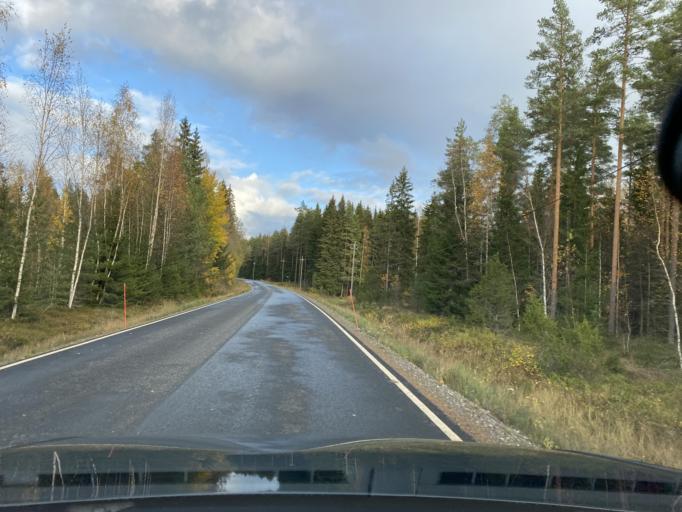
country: FI
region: Pirkanmaa
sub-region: Lounais-Pirkanmaa
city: Punkalaidun
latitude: 61.0579
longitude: 23.2099
